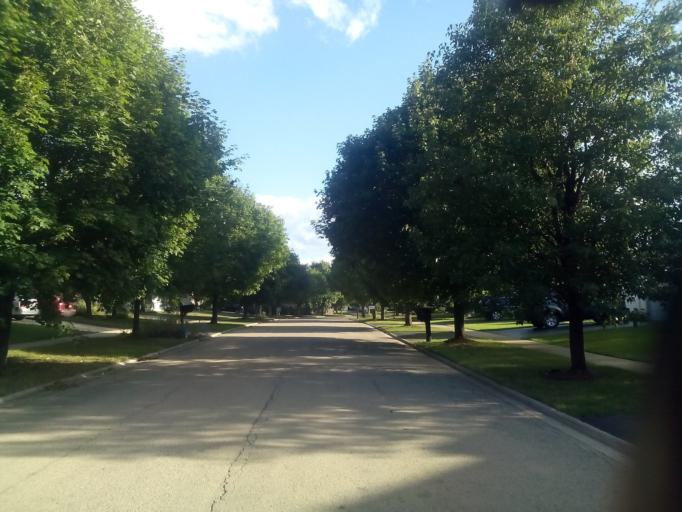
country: US
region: Illinois
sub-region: Will County
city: Plainfield
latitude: 41.6907
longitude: -88.1591
